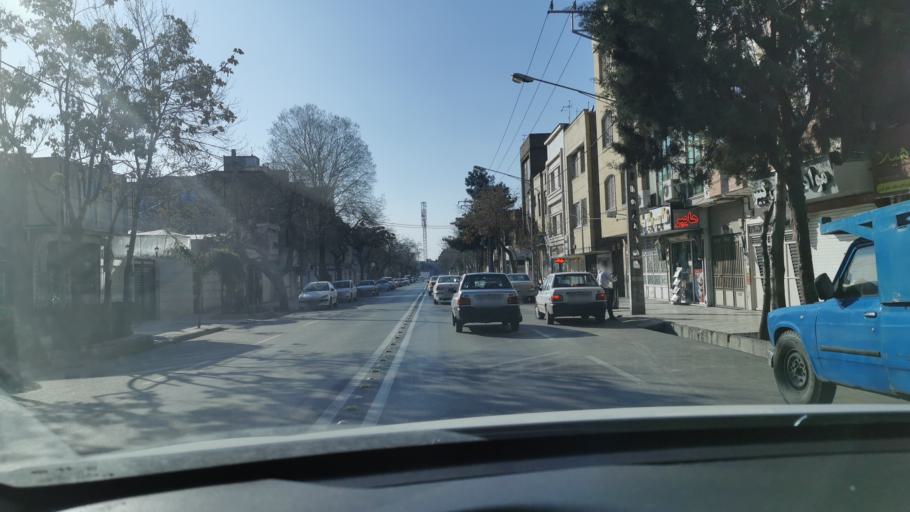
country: IR
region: Razavi Khorasan
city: Mashhad
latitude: 36.2784
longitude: 59.5746
